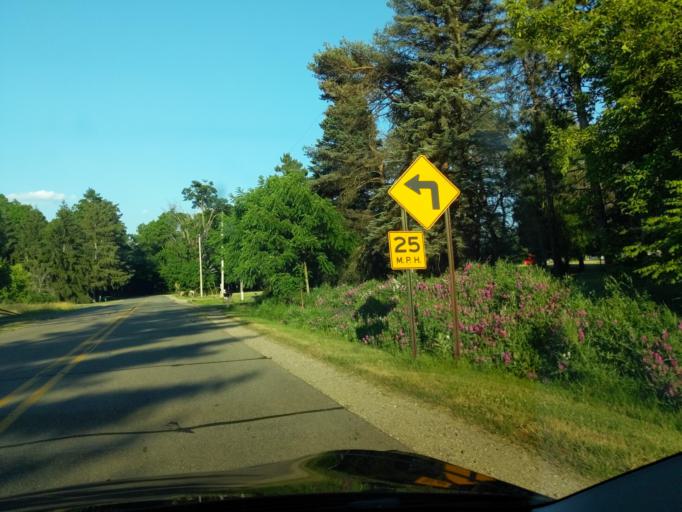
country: US
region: Michigan
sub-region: Eaton County
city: Dimondale
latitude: 42.6400
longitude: -84.6589
